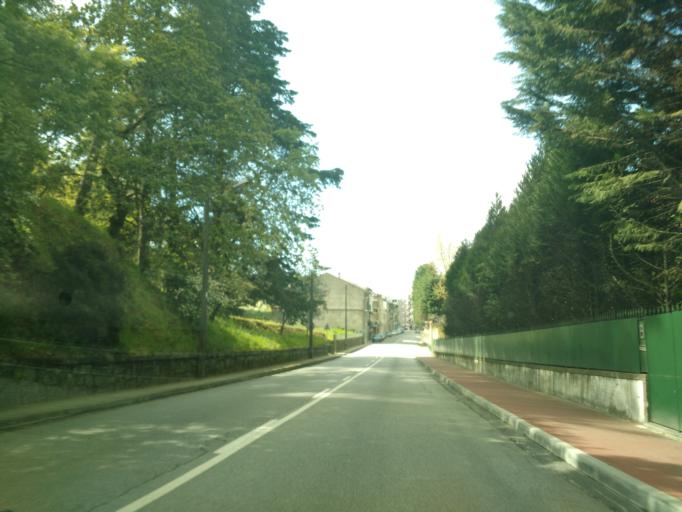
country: PT
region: Braga
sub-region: Braga
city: Braga
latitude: 41.5403
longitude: -8.4122
